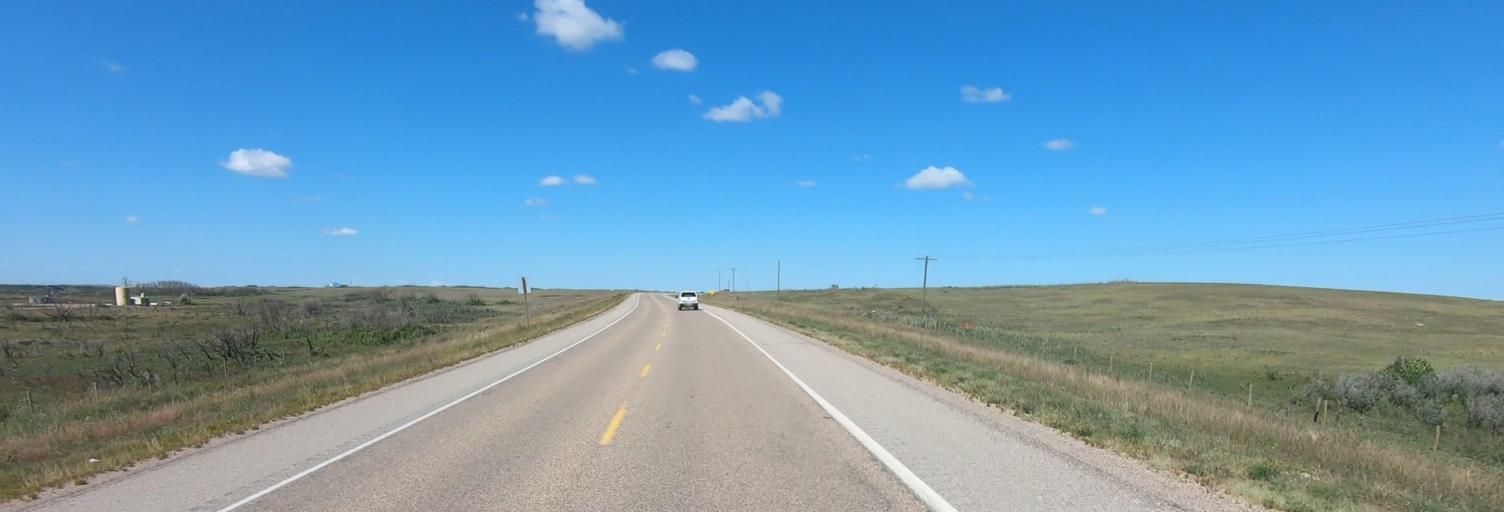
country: CA
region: Alberta
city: Strathmore
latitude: 50.8711
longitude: -113.1569
